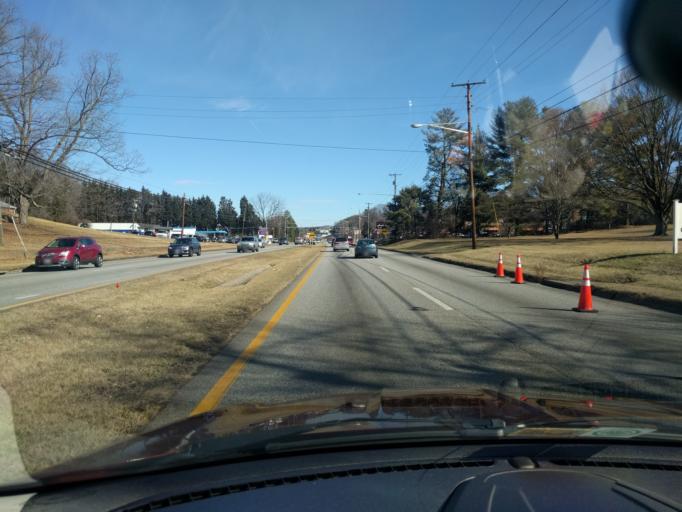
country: US
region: Virginia
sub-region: Roanoke County
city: Vinton
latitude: 37.2942
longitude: -79.9033
